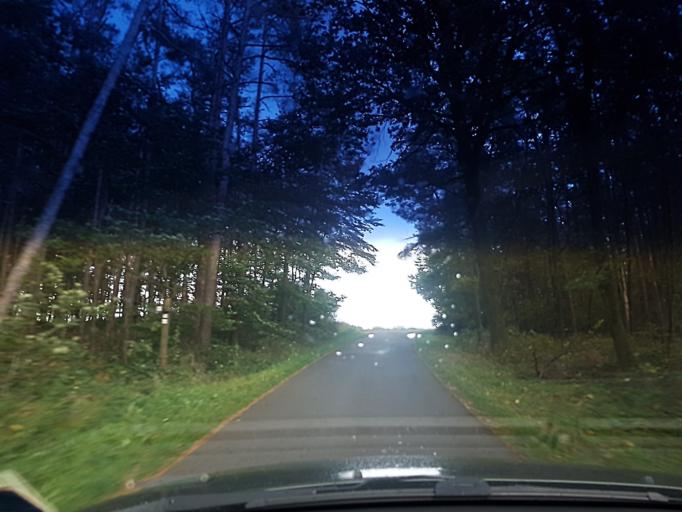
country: DE
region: Bavaria
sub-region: Regierungsbezirk Mittelfranken
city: Burghaslach
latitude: 49.7499
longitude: 10.5800
